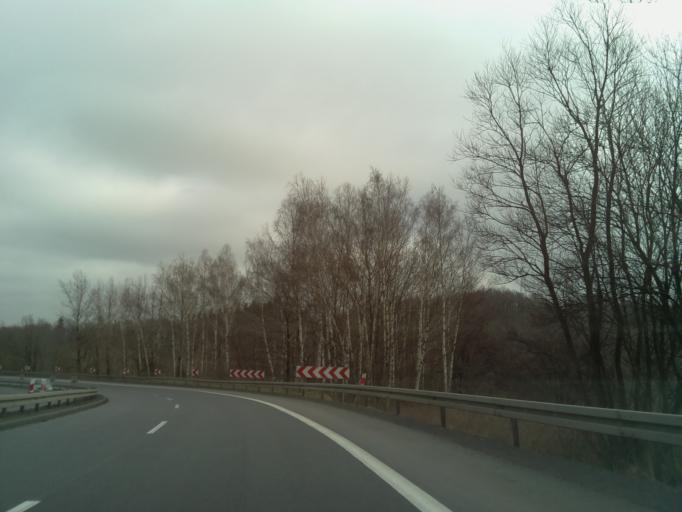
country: PL
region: Lower Silesian Voivodeship
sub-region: Powiat swidnicki
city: Swiebodzice
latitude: 50.8456
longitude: 16.3199
